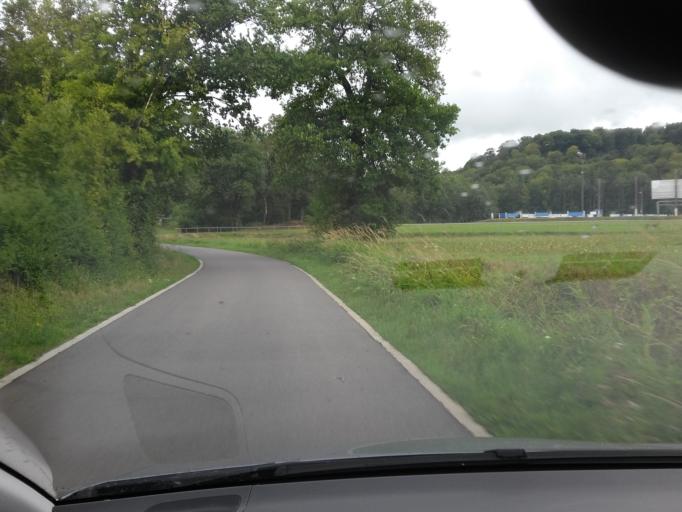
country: BE
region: Wallonia
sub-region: Province du Luxembourg
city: Arlon
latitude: 49.7220
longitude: 5.8160
